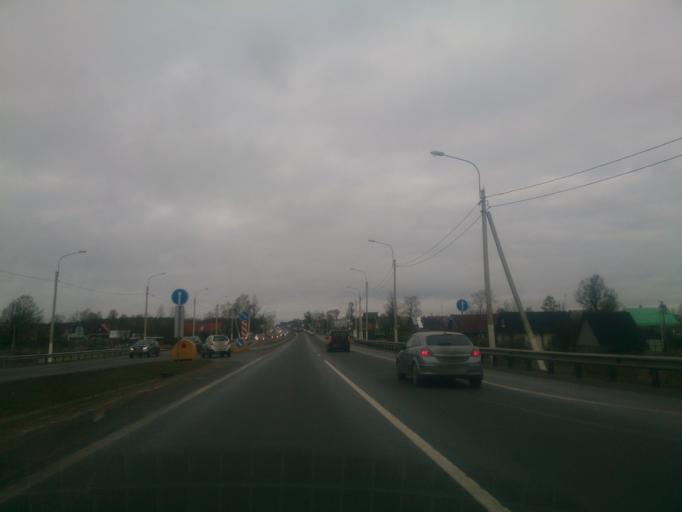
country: RU
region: Leningrad
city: Ul'yanovka
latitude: 59.6147
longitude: 30.7428
